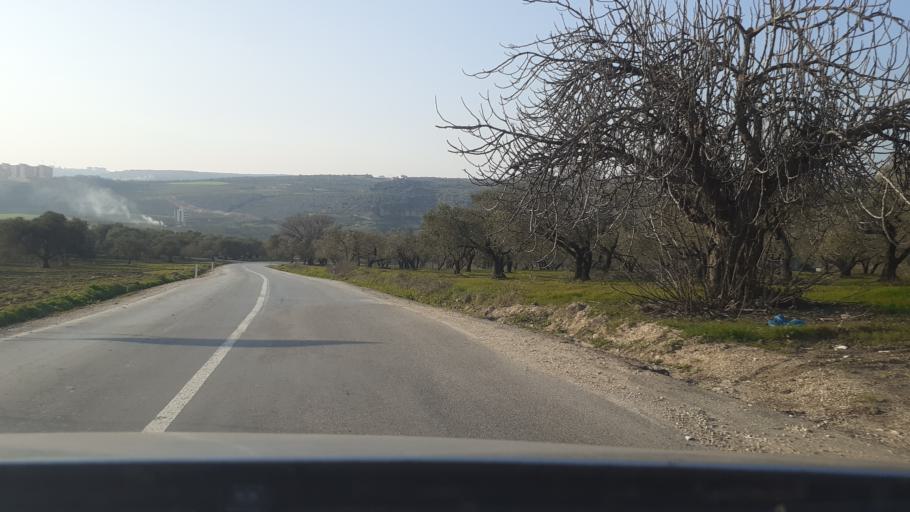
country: TR
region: Hatay
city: Oymakli
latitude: 36.1139
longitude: 36.2857
